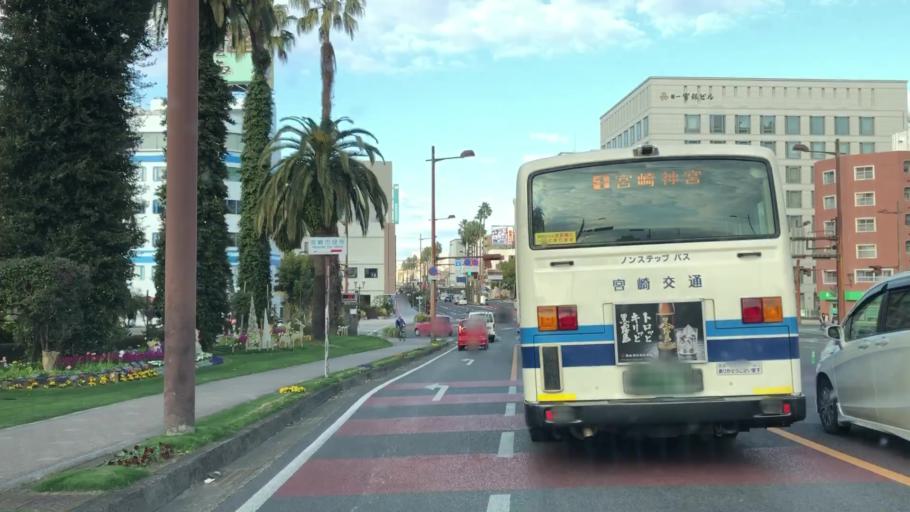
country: JP
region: Miyazaki
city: Miyazaki-shi
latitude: 31.9078
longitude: 131.4212
